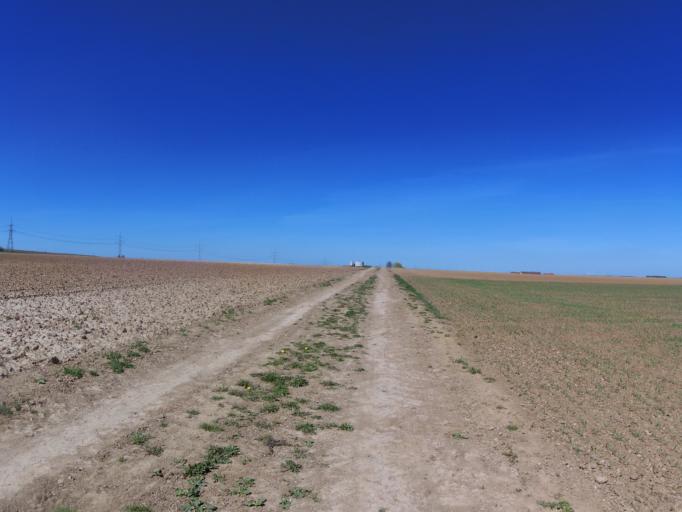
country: DE
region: Bavaria
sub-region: Regierungsbezirk Unterfranken
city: Biebelried
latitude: 49.8095
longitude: 10.0935
